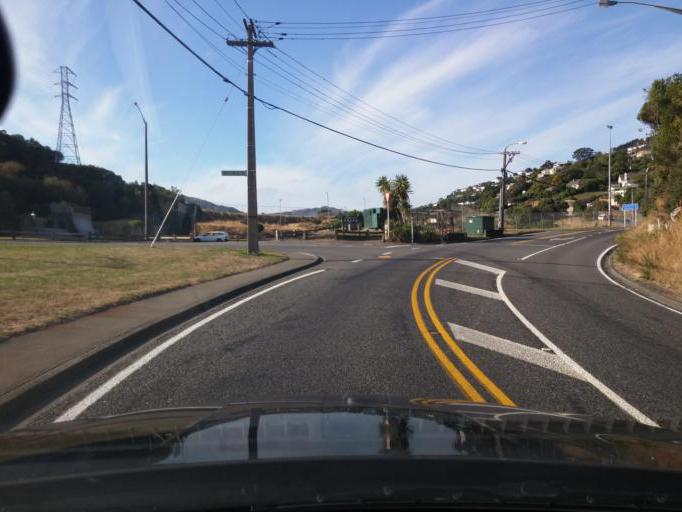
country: NZ
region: Wellington
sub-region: Wellington City
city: Kelburn
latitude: -41.2803
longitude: 174.7540
